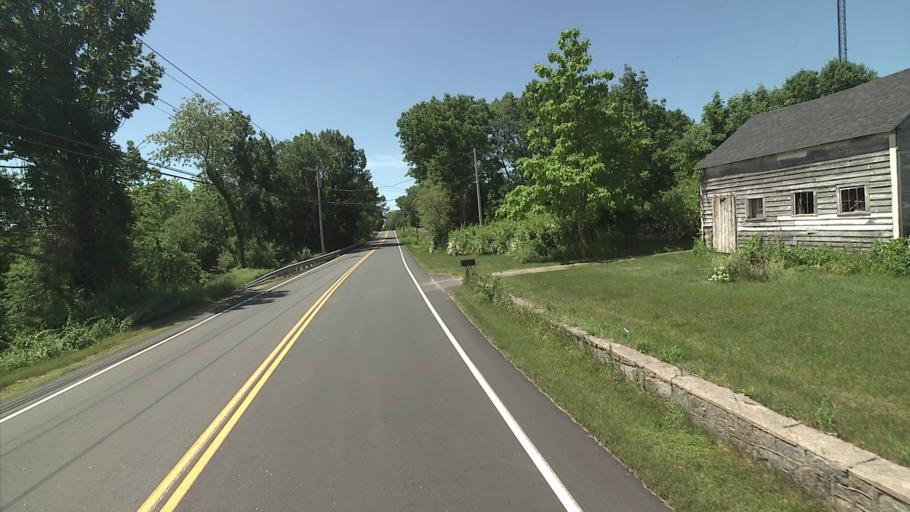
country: US
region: Connecticut
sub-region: Windham County
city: Moosup
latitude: 41.6626
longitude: -71.8462
